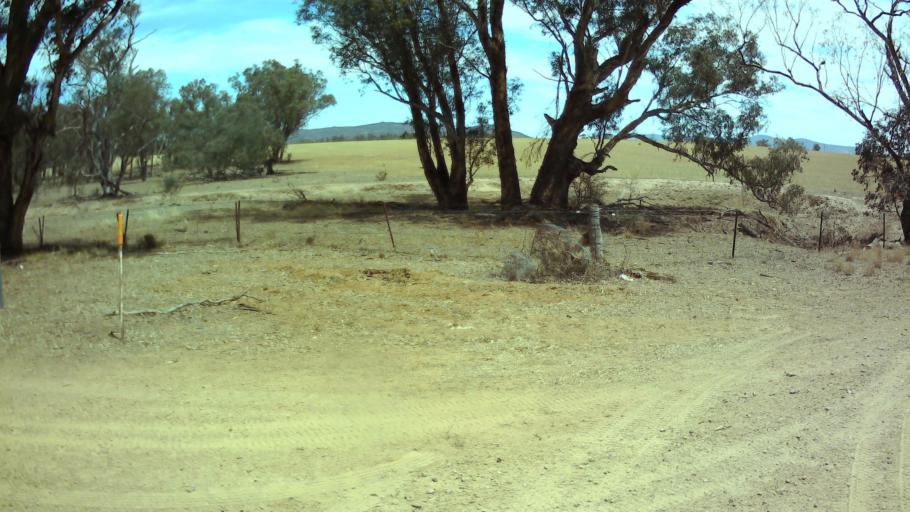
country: AU
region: New South Wales
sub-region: Weddin
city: Grenfell
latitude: -33.7583
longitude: 148.1431
